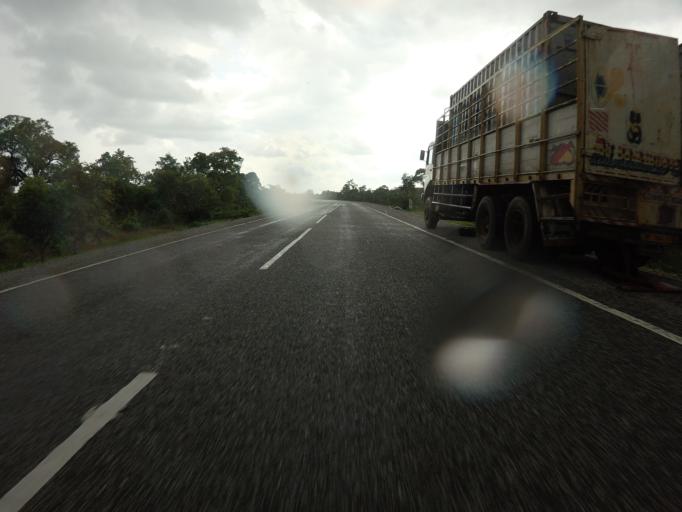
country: GH
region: Northern
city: Tamale
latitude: 9.1215
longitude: -1.6448
